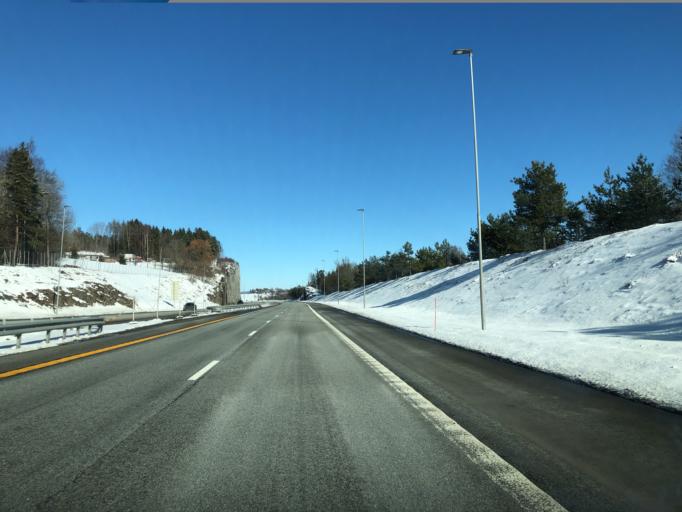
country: NO
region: Vestfold
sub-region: Sande
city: Sande
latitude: 59.6242
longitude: 10.1974
